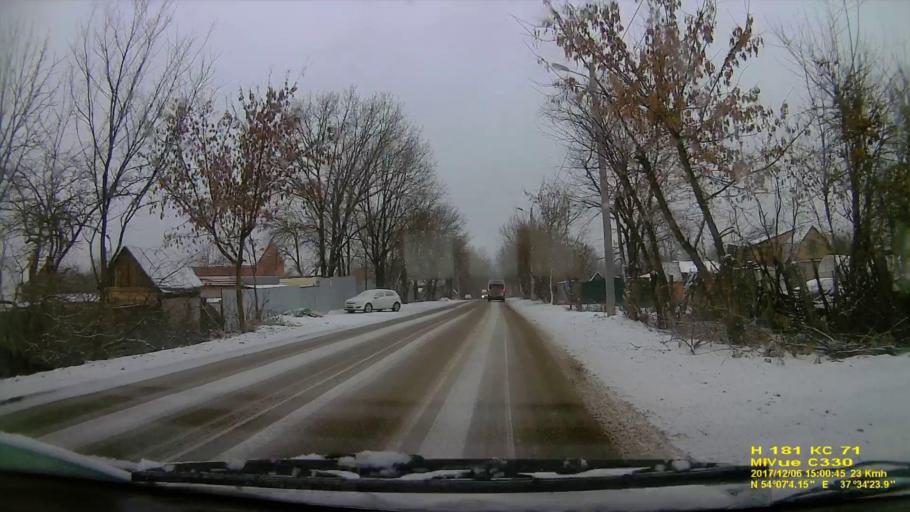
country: RU
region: Tula
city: Mendeleyevskiy
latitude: 54.1179
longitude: 37.5731
